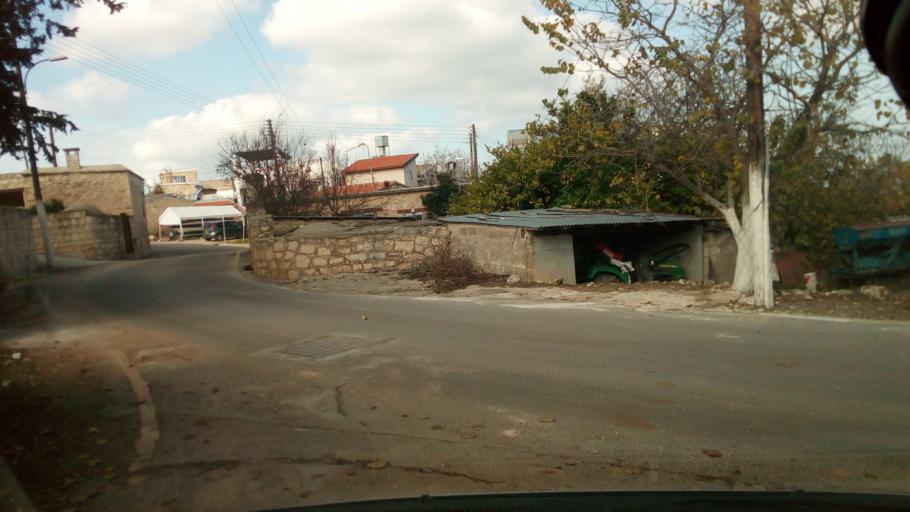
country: CY
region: Pafos
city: Polis
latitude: 34.9629
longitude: 32.3991
